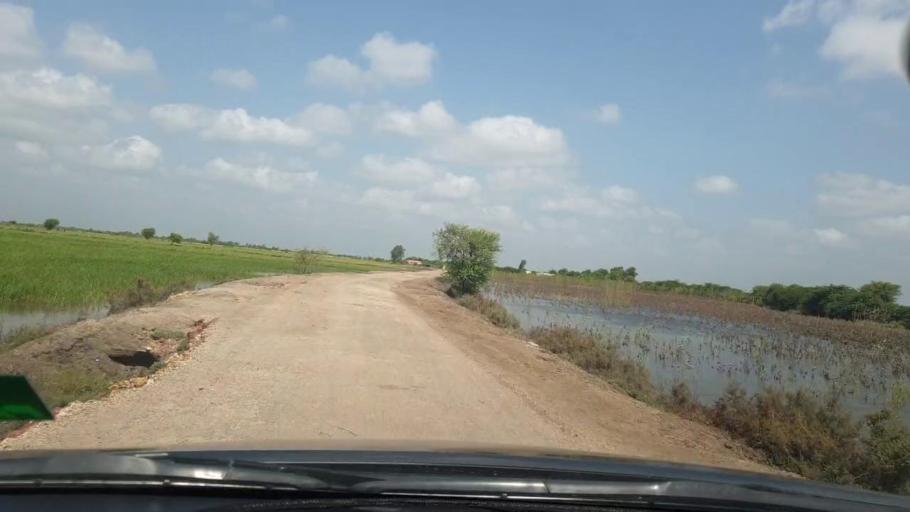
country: PK
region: Sindh
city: Tando Bago
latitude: 24.8628
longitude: 69.0577
